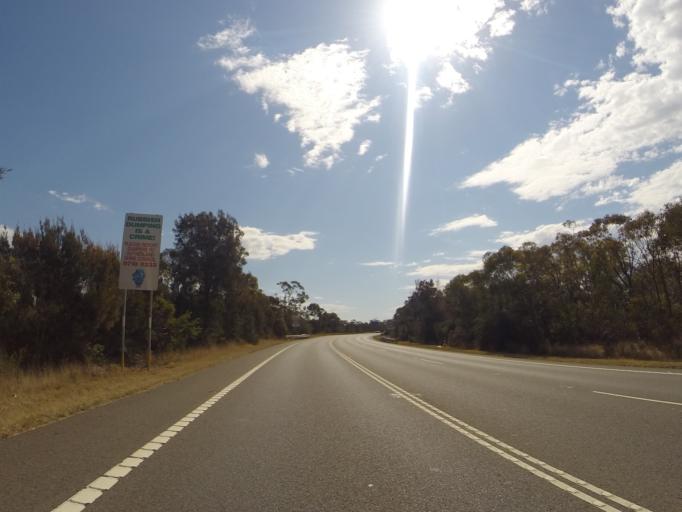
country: AU
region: New South Wales
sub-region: Sutherland Shire
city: Engadine
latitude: -34.0435
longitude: 150.9597
